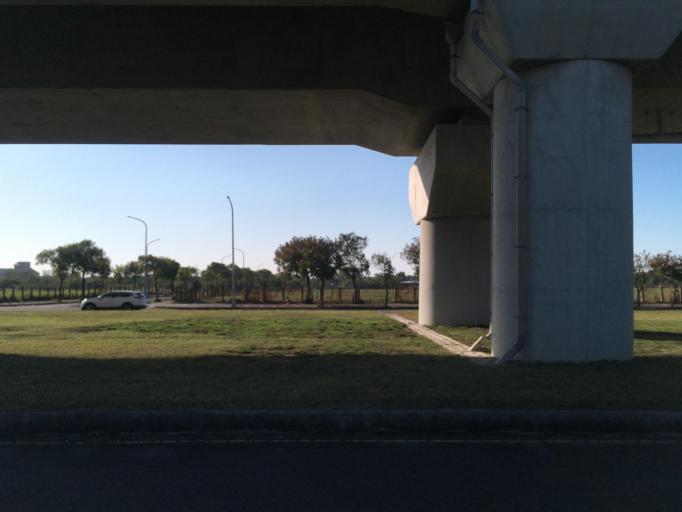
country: TW
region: Taiwan
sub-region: Chiayi
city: Taibao
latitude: 23.4537
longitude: 120.3238
